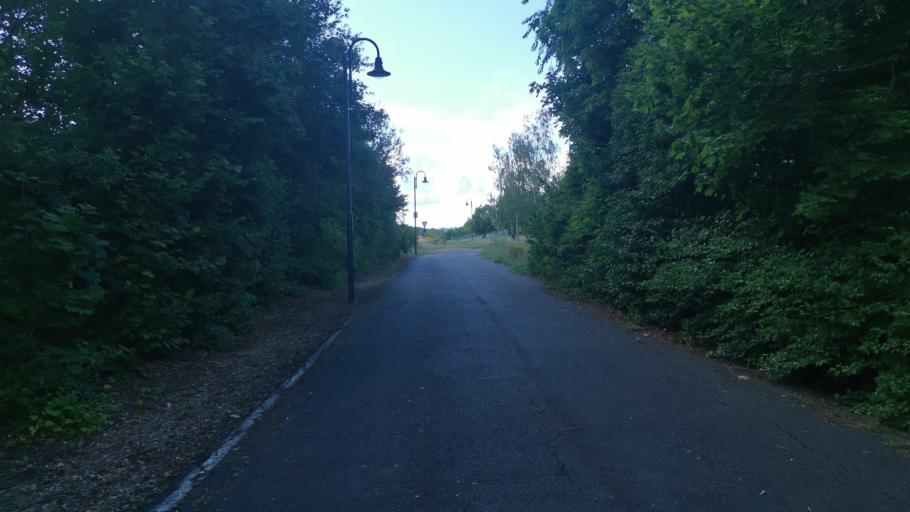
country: DE
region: Rheinland-Pfalz
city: Rudesheim
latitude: 49.8466
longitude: 7.8062
